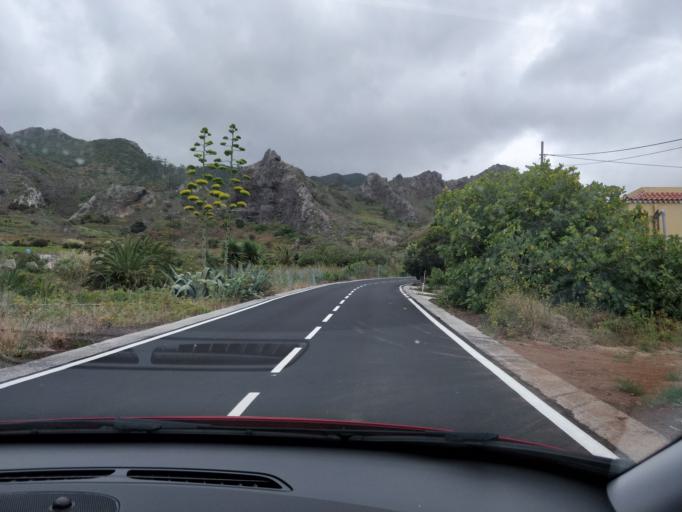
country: ES
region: Canary Islands
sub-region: Provincia de Santa Cruz de Tenerife
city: Tanque
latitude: 28.3509
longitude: -16.8444
